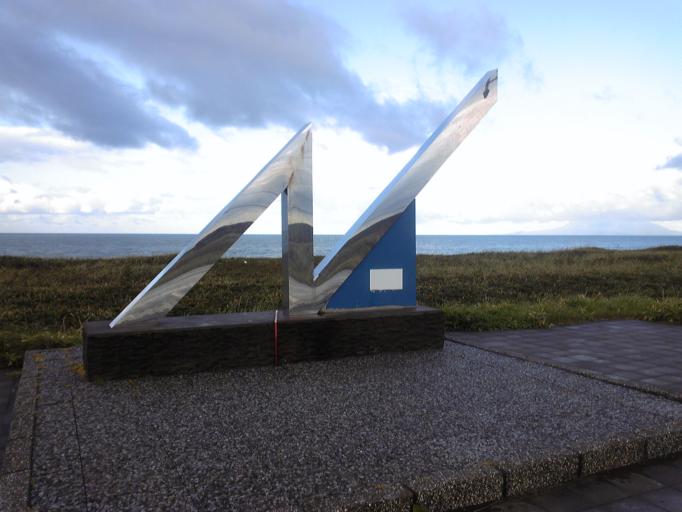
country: JP
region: Hokkaido
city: Makubetsu
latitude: 45.0023
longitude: 141.6815
